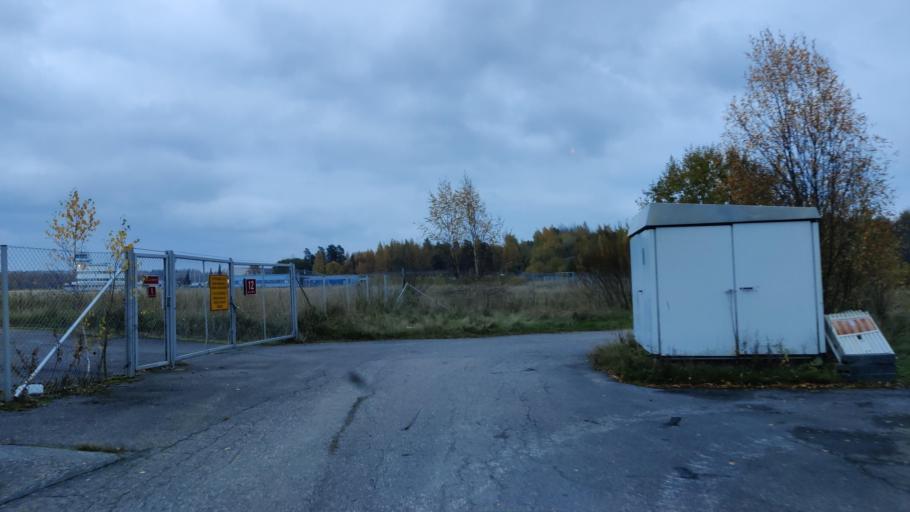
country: FI
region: Uusimaa
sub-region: Helsinki
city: Vantaa
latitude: 60.2480
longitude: 25.0387
